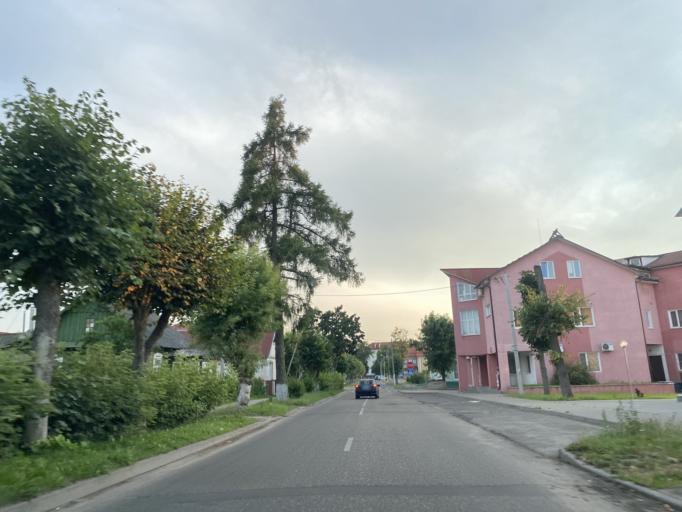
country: BY
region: Brest
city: Ivatsevichy
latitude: 52.7113
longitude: 25.3449
